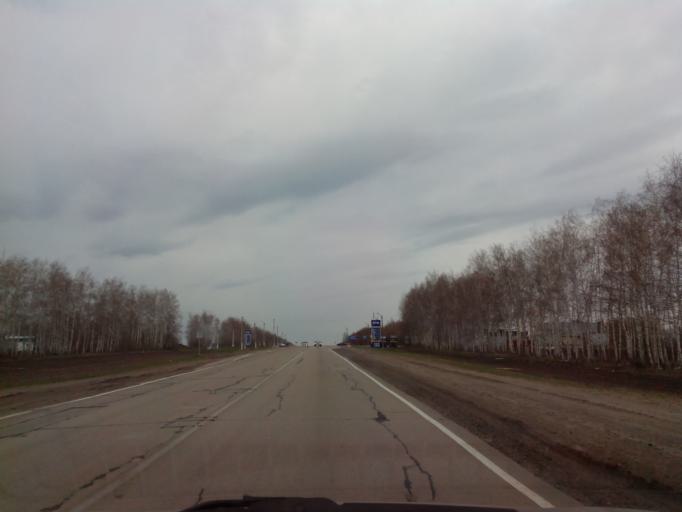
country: RU
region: Tambov
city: Znamenka
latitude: 52.4007
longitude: 41.3923
